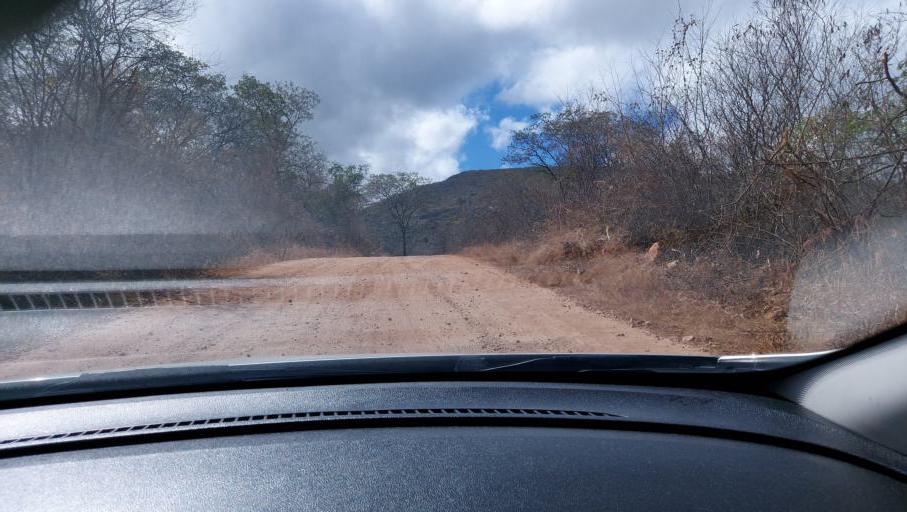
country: BR
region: Bahia
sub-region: Oliveira Dos Brejinhos
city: Beira Rio
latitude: -12.0977
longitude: -42.5516
